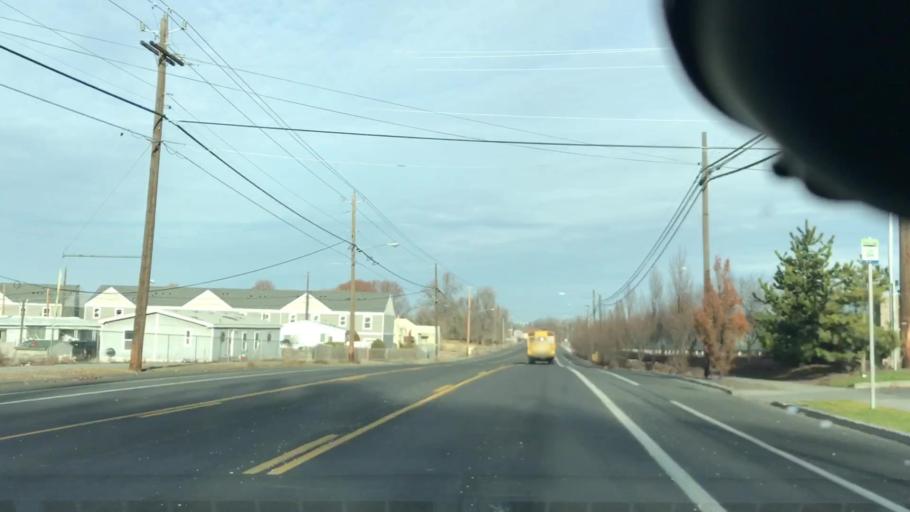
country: US
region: Washington
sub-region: Grant County
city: Moses Lake
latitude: 47.1217
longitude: -119.2744
